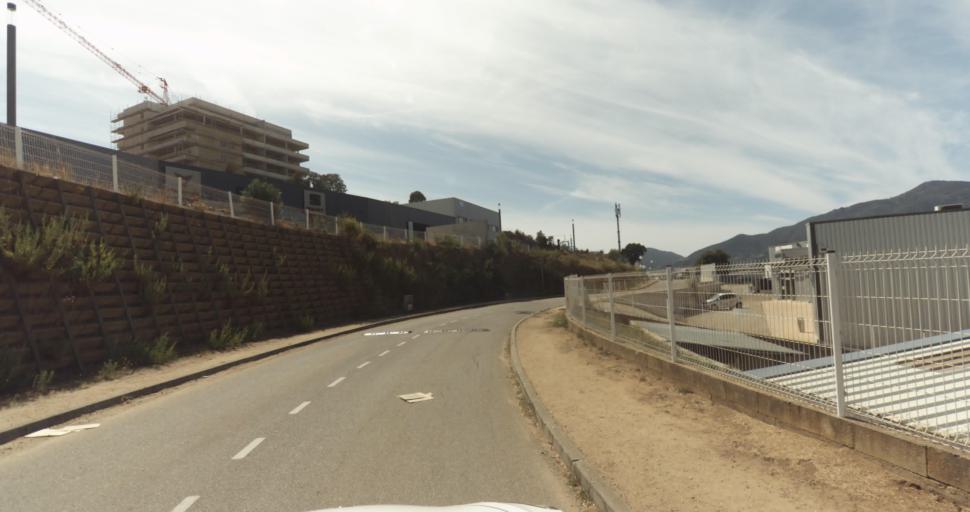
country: FR
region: Corsica
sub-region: Departement de la Corse-du-Sud
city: Alata
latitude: 41.9489
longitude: 8.7709
